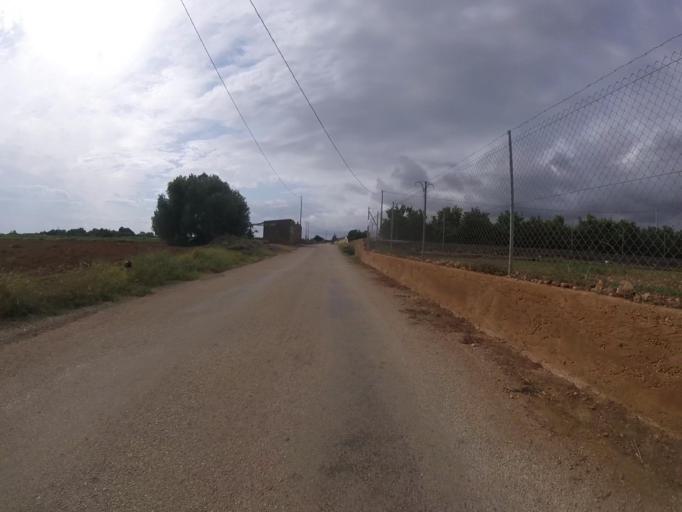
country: ES
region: Valencia
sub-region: Provincia de Castello
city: Torreblanca
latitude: 40.1986
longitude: 0.1790
